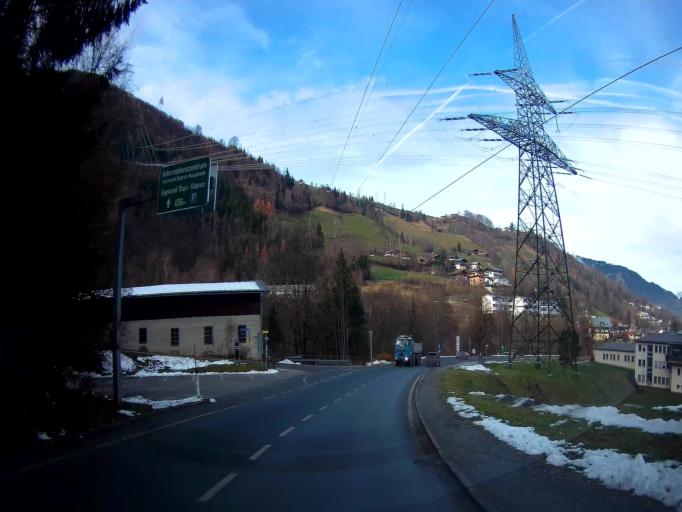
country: AT
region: Salzburg
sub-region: Politischer Bezirk Zell am See
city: Kaprun
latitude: 47.2589
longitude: 12.7405
